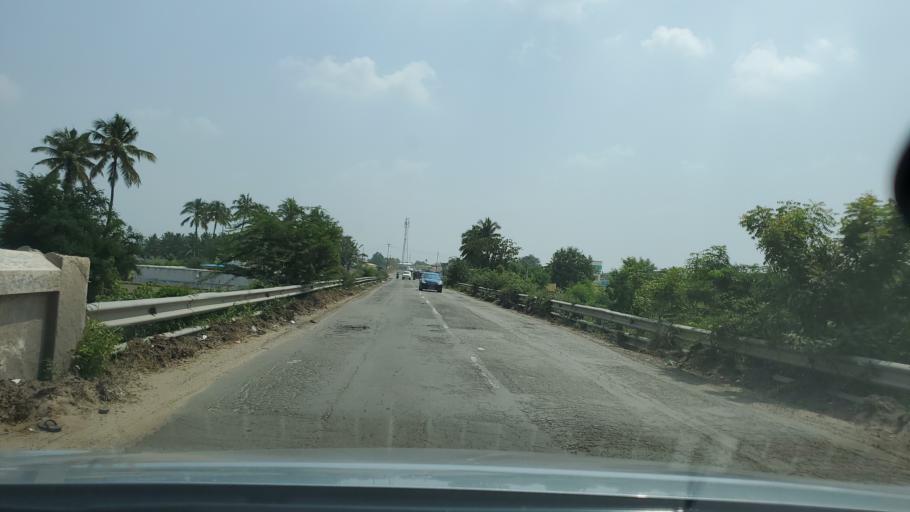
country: IN
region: Tamil Nadu
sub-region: Tiruppur
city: Dharapuram
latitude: 10.7718
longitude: 77.5107
